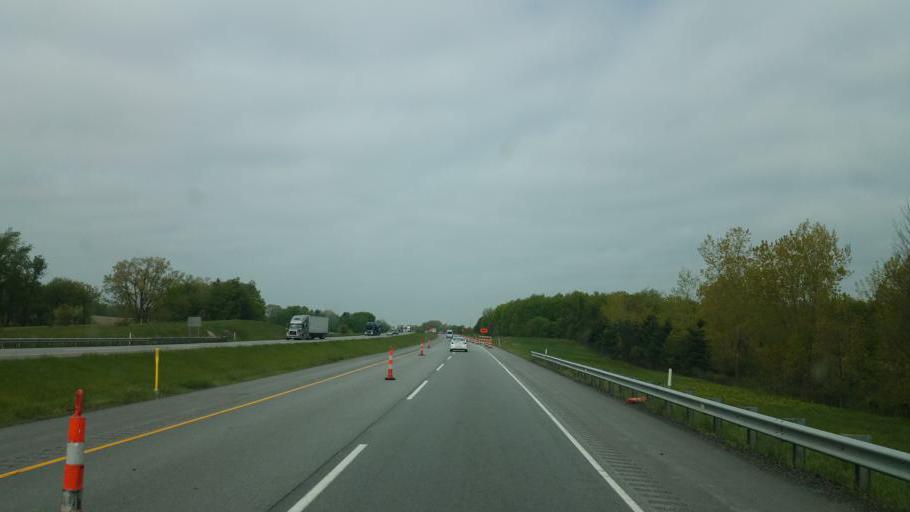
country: US
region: Indiana
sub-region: LaPorte County
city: LaPorte
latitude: 41.6746
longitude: -86.6912
